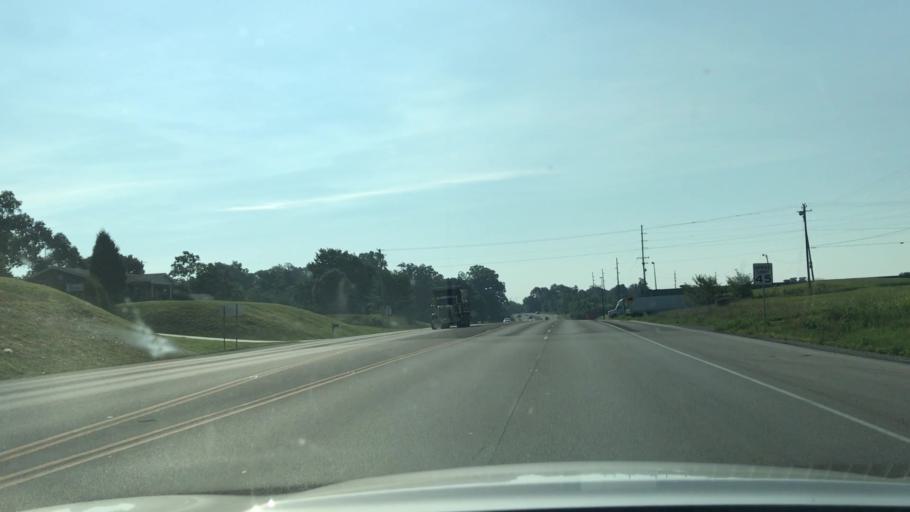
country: US
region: Kentucky
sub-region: Barren County
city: Glasgow
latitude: 37.0117
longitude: -85.9519
